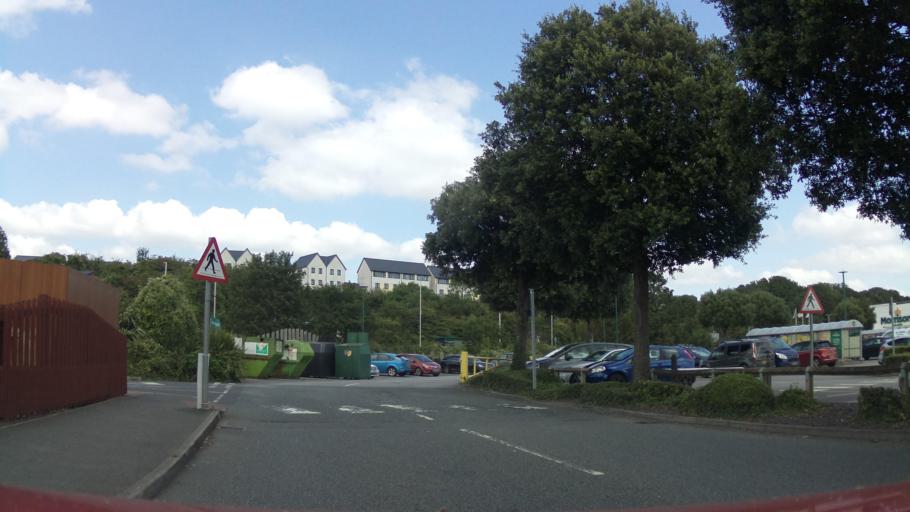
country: GB
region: England
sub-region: Plymouth
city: Plymstock
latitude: 50.3636
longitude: -4.0994
